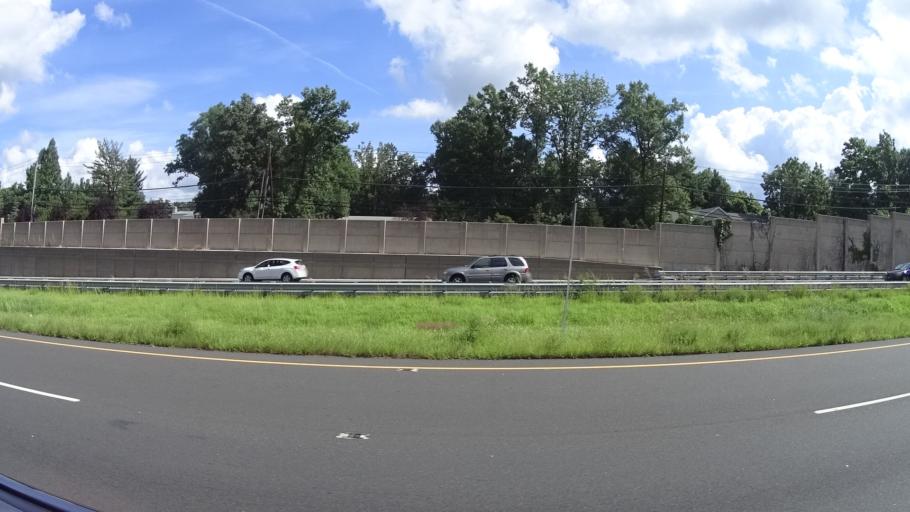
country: US
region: New Jersey
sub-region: Union County
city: Summit
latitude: 40.7324
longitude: -74.3527
